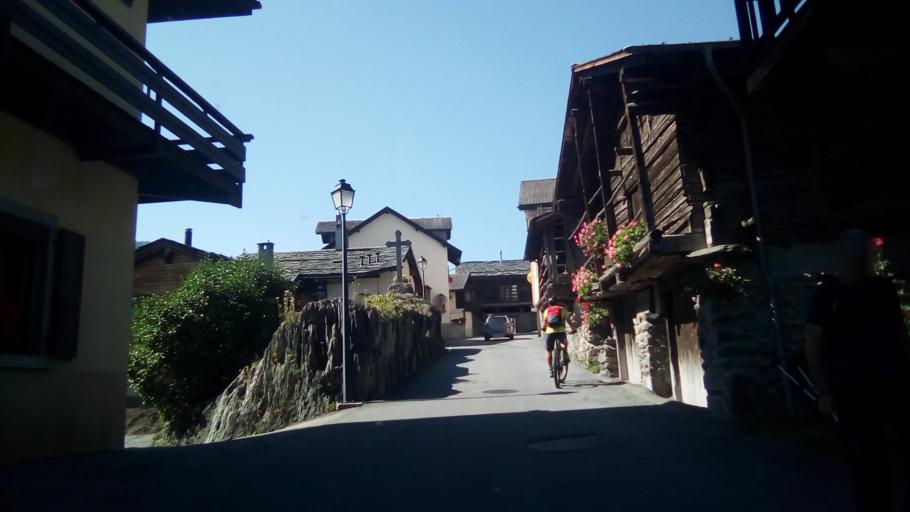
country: CH
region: Valais
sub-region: Saint-Maurice District
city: Salvan
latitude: 46.1119
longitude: 7.0081
